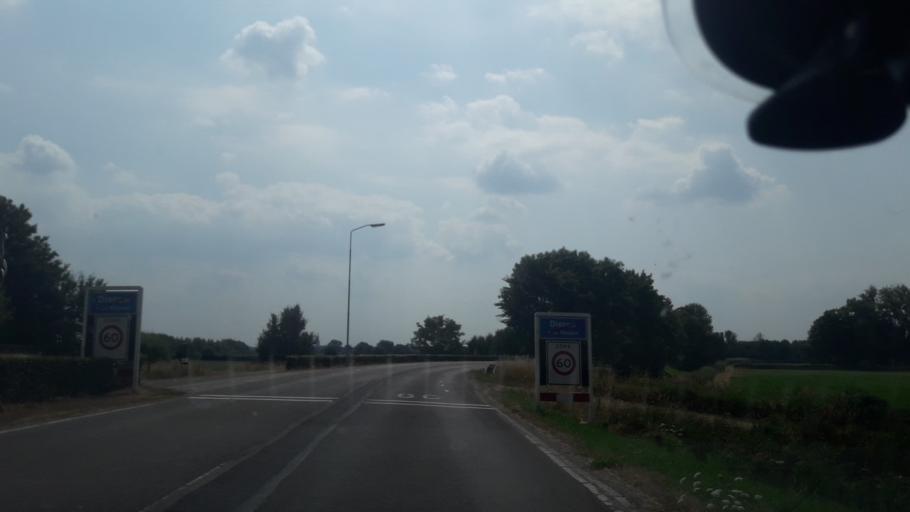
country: NL
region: Gelderland
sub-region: Gemeente Rheden
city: Dieren
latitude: 52.0393
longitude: 6.1055
